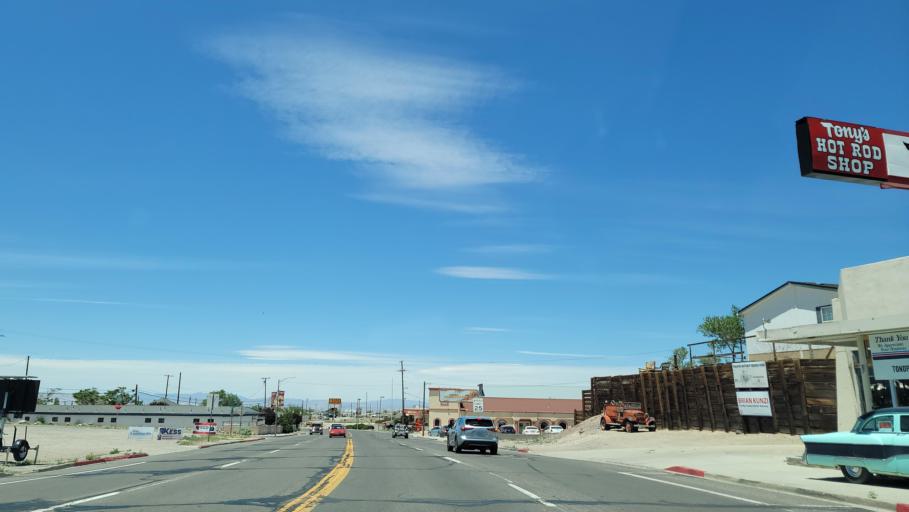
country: US
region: Nevada
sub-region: Nye County
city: Tonopah
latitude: 38.0702
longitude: -117.2319
